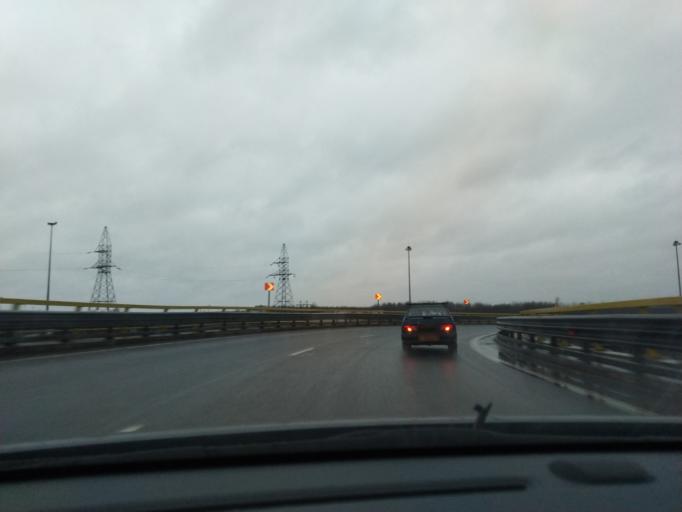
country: RU
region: St.-Petersburg
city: Sosnovaya Polyana
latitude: 59.8006
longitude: 30.1534
